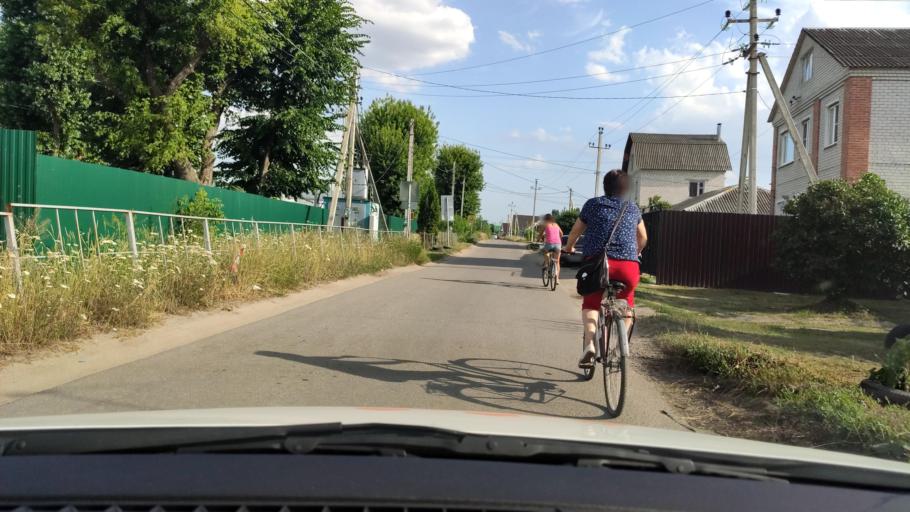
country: RU
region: Voronezj
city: Novaya Usman'
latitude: 51.6337
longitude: 39.4142
